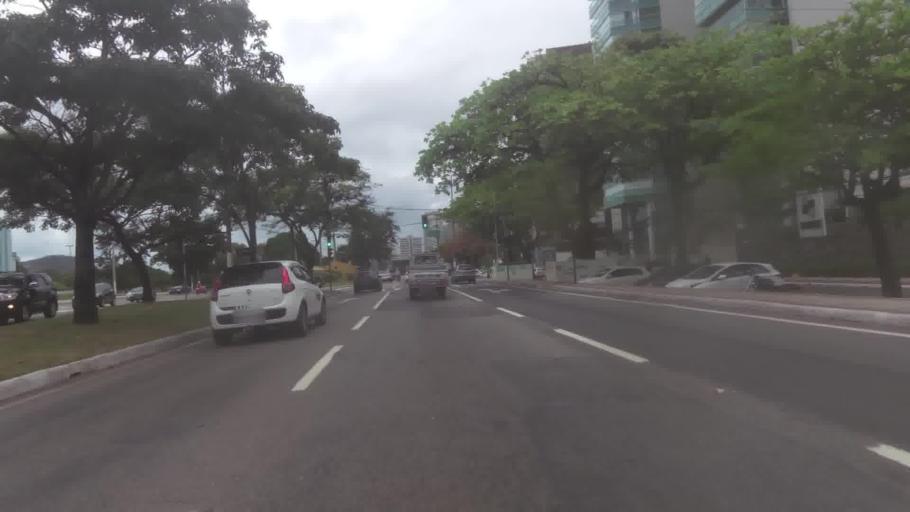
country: BR
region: Espirito Santo
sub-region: Vila Velha
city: Vila Velha
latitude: -20.3020
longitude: -40.2919
